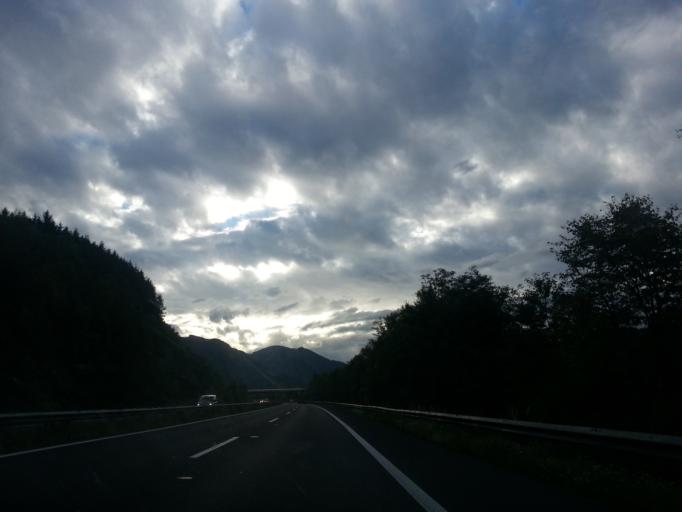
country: AT
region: Styria
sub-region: Politischer Bezirk Leoben
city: Mautern in Steiermark
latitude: 47.3949
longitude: 14.8546
